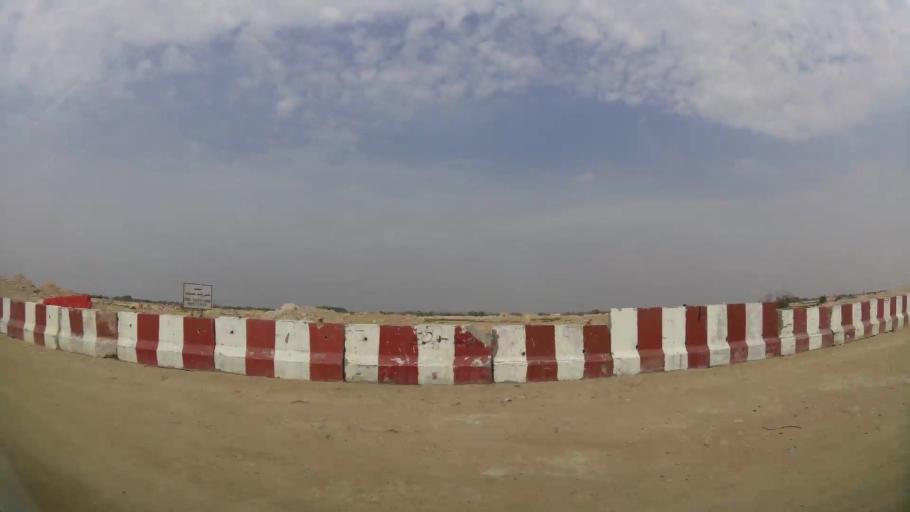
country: AE
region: Abu Dhabi
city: Abu Dhabi
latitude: 24.6518
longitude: 54.7371
